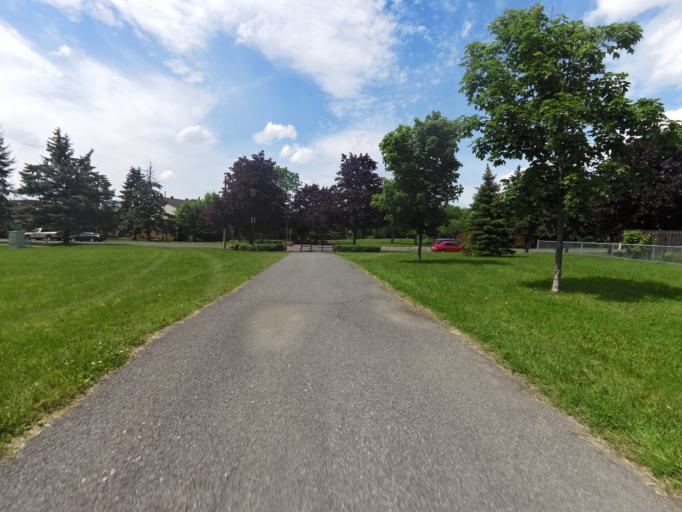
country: CA
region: Ontario
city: Ottawa
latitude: 45.3593
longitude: -75.6433
